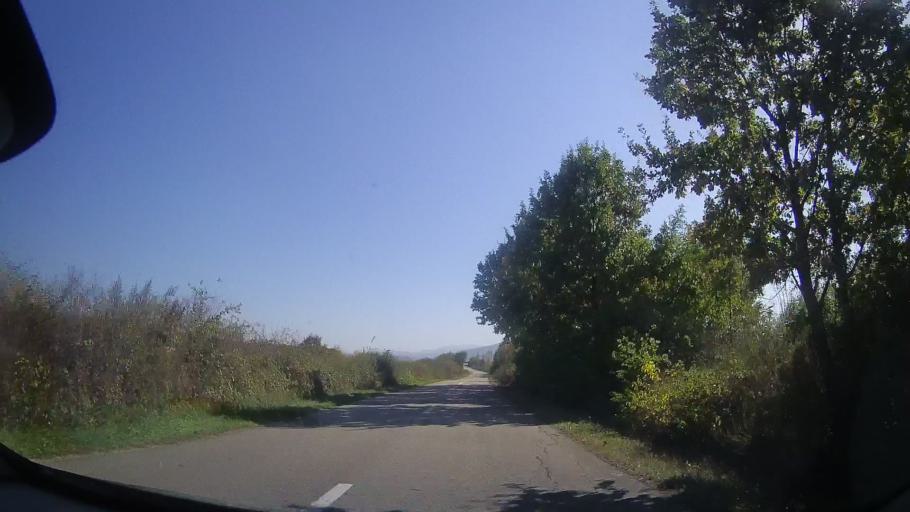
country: RO
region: Timis
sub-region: Comuna Traian Vuia
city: Traian Vuia
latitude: 45.7858
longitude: 22.0406
